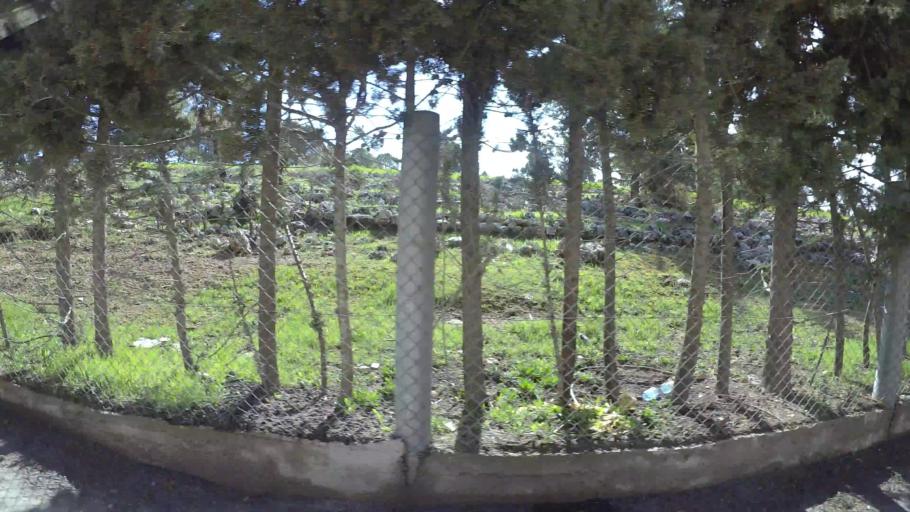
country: JO
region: Amman
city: Al Jubayhah
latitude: 32.0112
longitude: 35.8453
